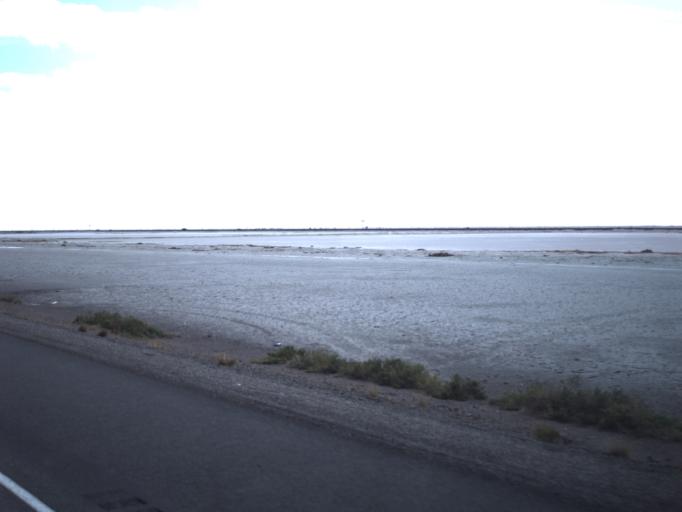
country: US
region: Utah
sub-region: Tooele County
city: Wendover
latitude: 40.7410
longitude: -113.9581
